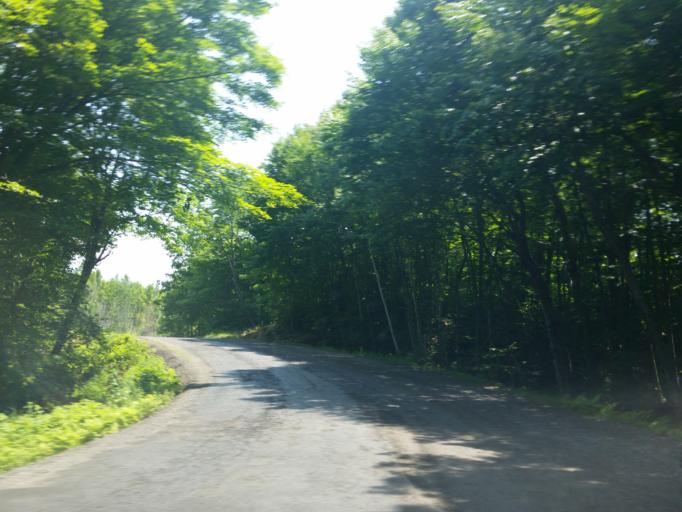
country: CA
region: Ontario
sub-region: Parry Sound District
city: Parry Sound
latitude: 45.4299
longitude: -80.0145
